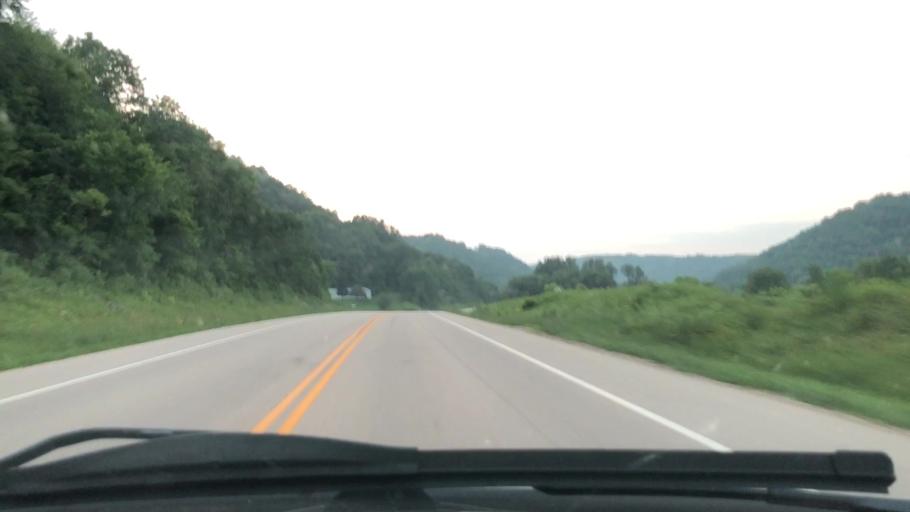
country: US
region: Wisconsin
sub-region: Richland County
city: Richland Center
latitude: 43.3566
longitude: -90.5557
